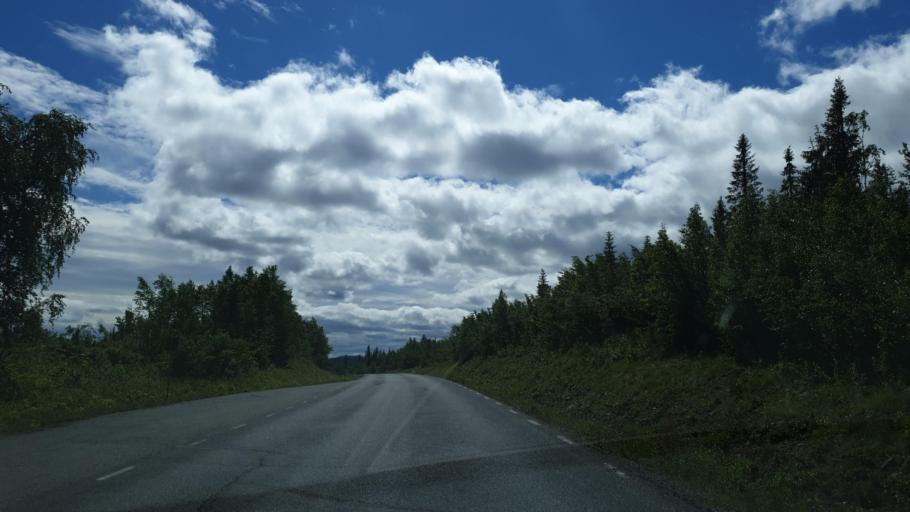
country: SE
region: Vaesterbotten
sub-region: Vilhelmina Kommun
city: Sjoberg
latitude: 64.9964
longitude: 15.8361
